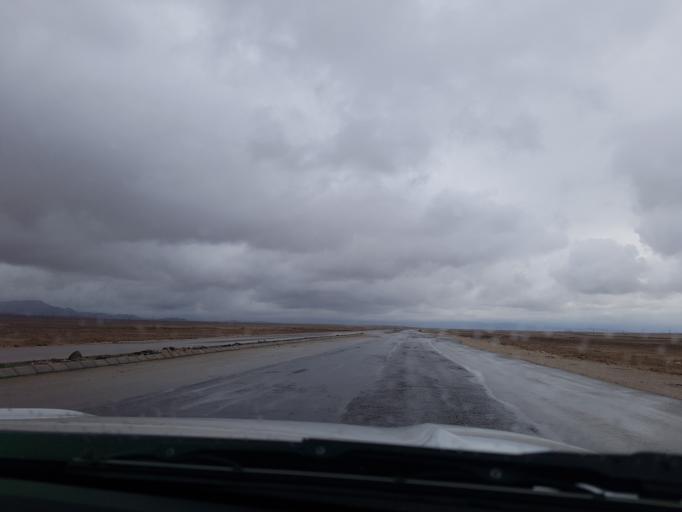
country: TM
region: Balkan
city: Balkanabat
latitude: 39.8865
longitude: 54.0416
